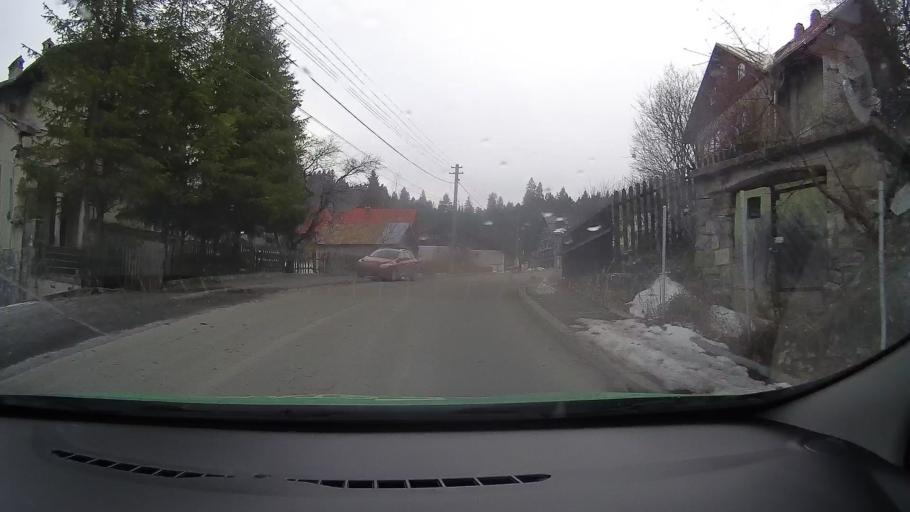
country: RO
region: Prahova
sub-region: Oras Sinaia
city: Sinaia
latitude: 45.3545
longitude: 25.5402
